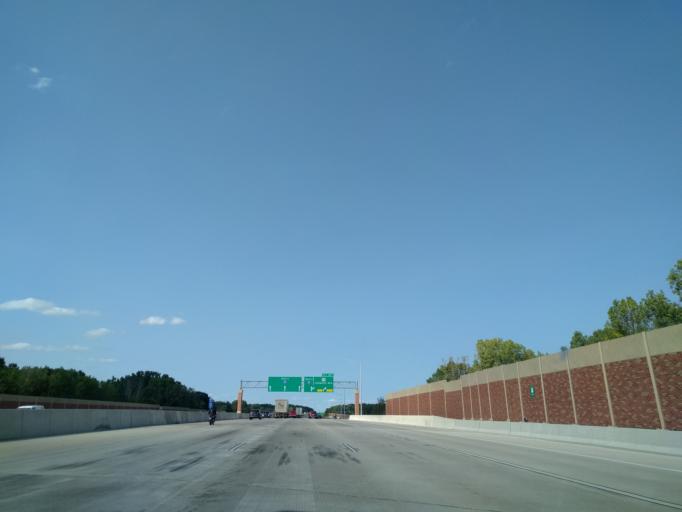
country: US
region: Wisconsin
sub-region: Brown County
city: Ashwaubenon
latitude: 44.5030
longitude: -88.0819
